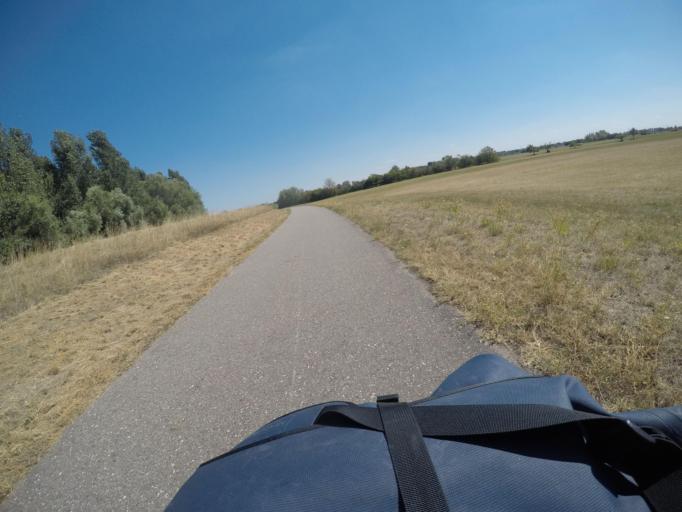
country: DE
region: Baden-Wuerttemberg
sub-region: Karlsruhe Region
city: Oberhausen-Rheinhausen
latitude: 49.2830
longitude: 8.4838
